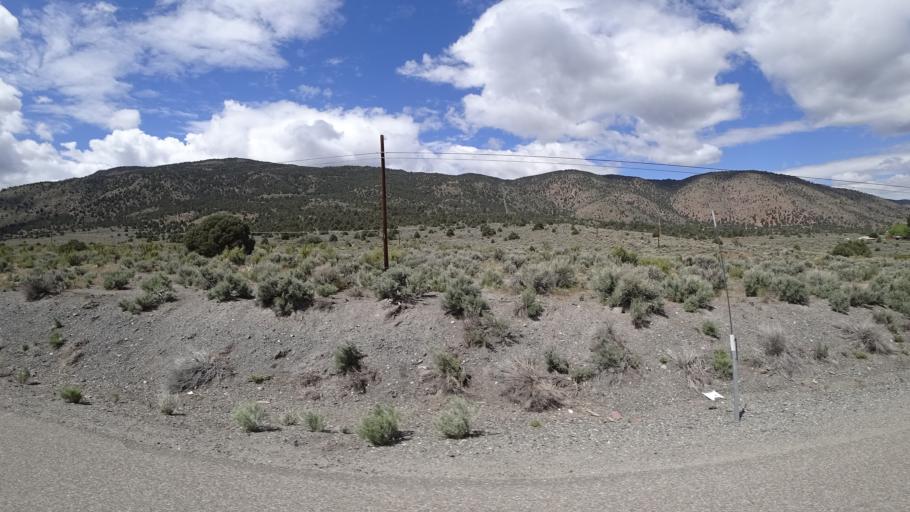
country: US
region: Nevada
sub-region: Lyon County
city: Smith Valley
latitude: 38.7191
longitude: -119.5542
